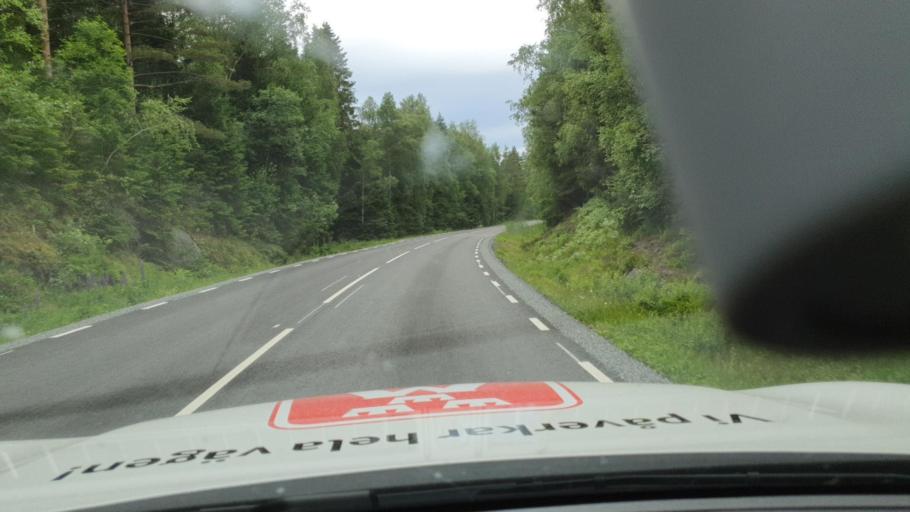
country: SE
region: OErebro
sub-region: Laxa Kommun
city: Laxa
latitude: 58.8738
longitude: 14.5128
